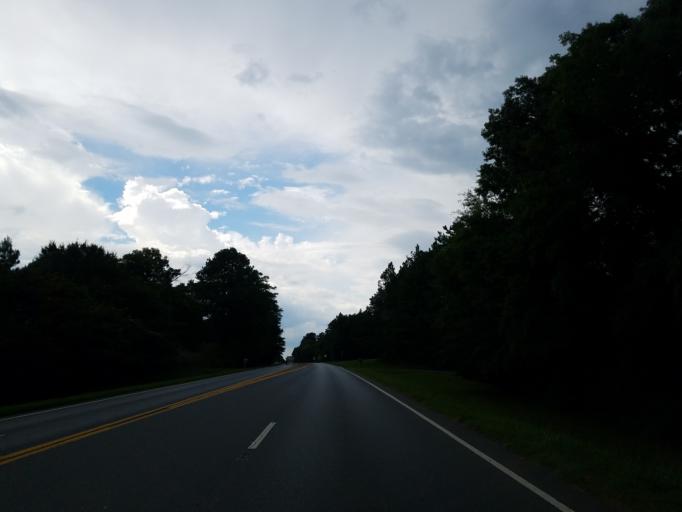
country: US
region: Georgia
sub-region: Bartow County
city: Adairsville
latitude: 34.3481
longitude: -84.9131
